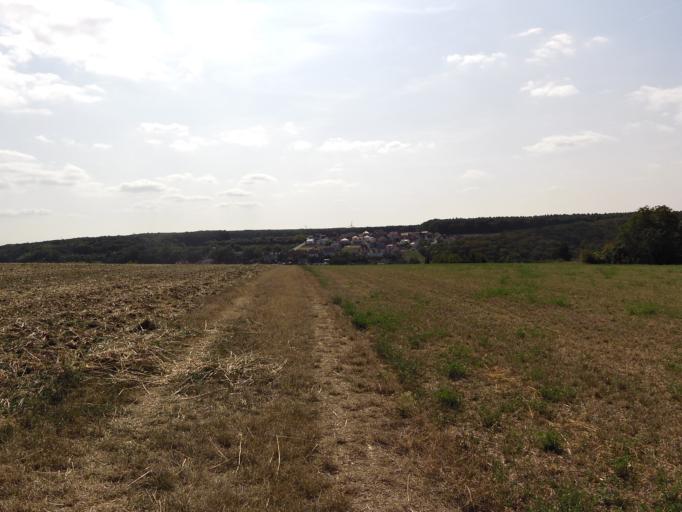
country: DE
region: Bavaria
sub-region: Regierungsbezirk Unterfranken
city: Theilheim
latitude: 49.7571
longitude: 10.0198
